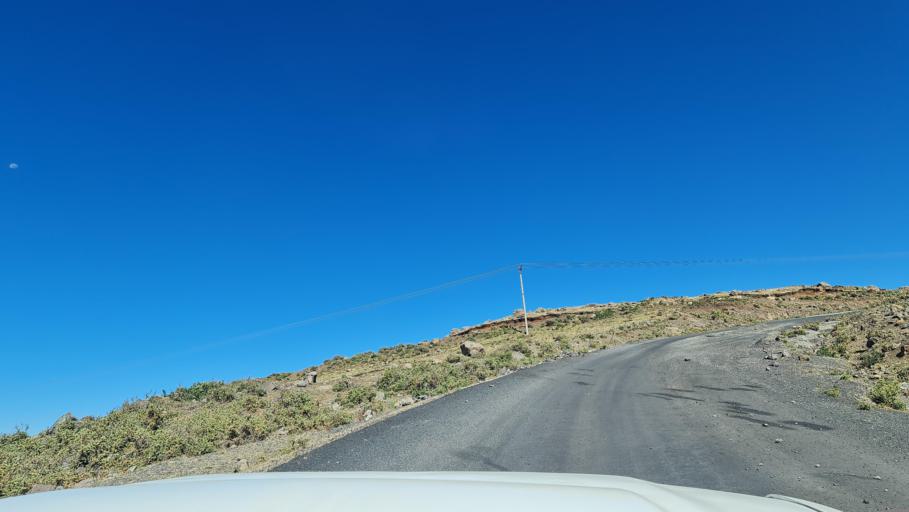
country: ET
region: Amhara
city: Debark'
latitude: 13.1392
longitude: 38.1770
